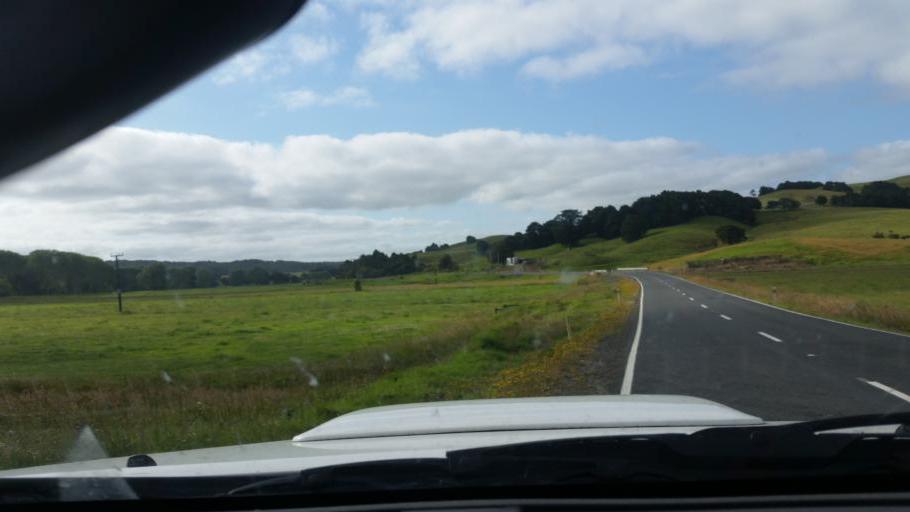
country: NZ
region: Northland
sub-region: Kaipara District
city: Dargaville
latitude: -35.8476
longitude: 173.8436
